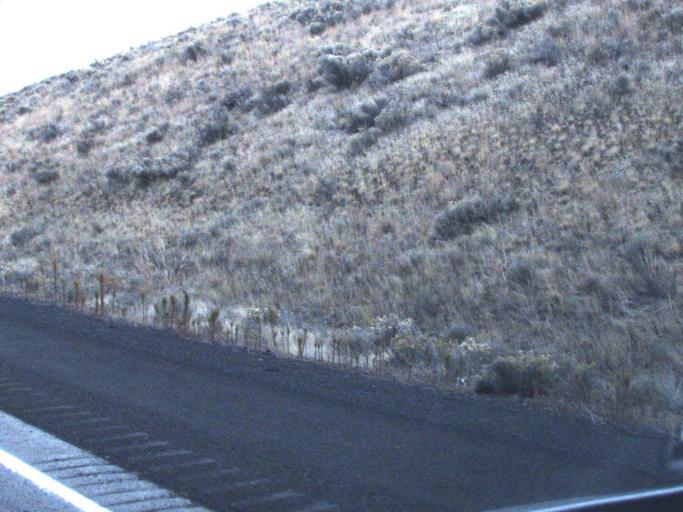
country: US
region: Washington
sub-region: Adams County
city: Ritzville
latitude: 47.0454
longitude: -118.4442
